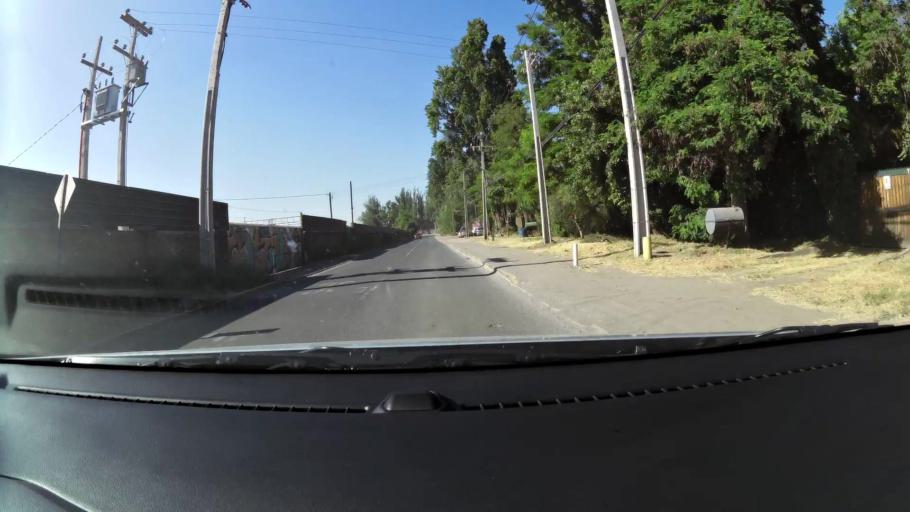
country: CL
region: Santiago Metropolitan
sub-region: Provincia de Maipo
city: San Bernardo
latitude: -33.5621
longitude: -70.6969
